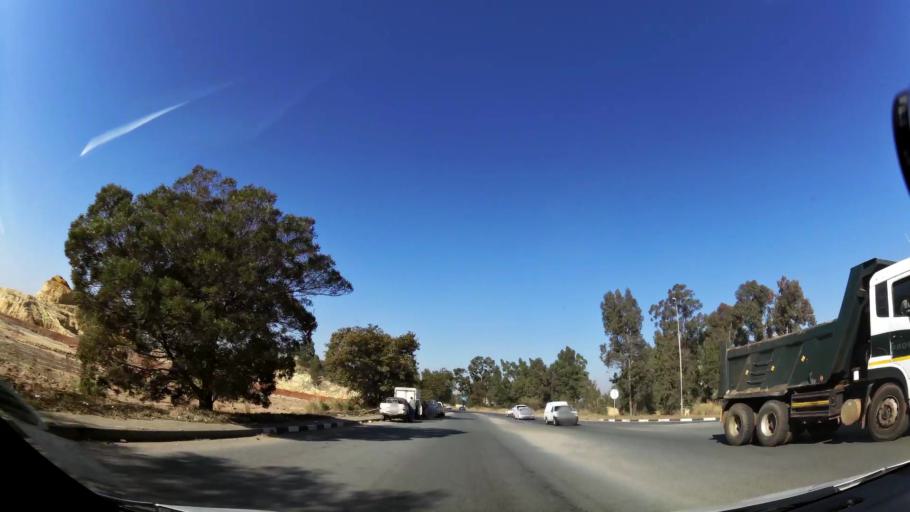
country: ZA
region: Gauteng
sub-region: Ekurhuleni Metropolitan Municipality
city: Germiston
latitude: -26.2151
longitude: 28.1145
